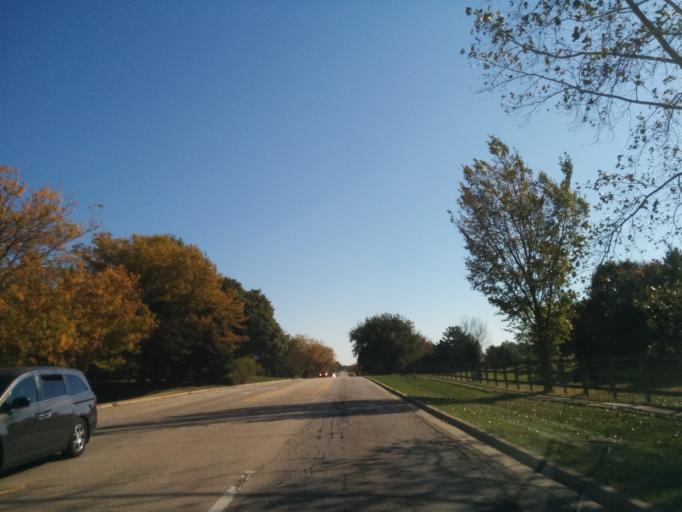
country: US
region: Illinois
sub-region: DuPage County
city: Carol Stream
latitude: 41.9518
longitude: -88.1608
